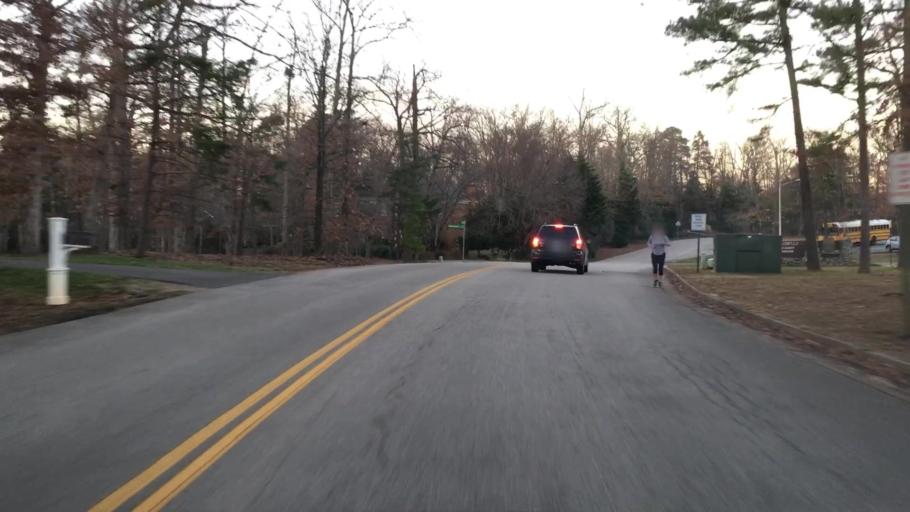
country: US
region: Virginia
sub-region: Chesterfield County
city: Bon Air
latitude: 37.5317
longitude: -77.6146
